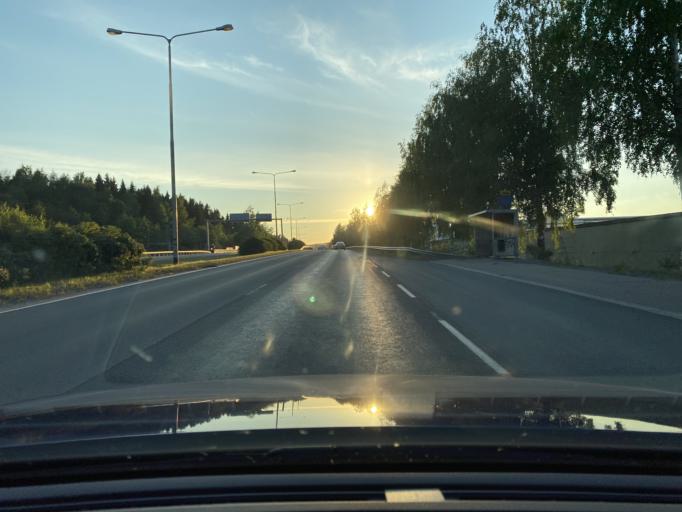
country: FI
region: Pirkanmaa
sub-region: Tampere
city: Pirkkala
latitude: 61.5154
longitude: 23.6613
